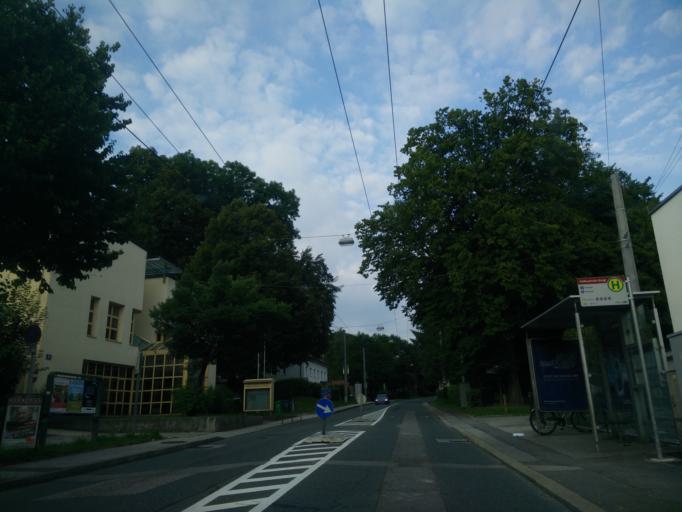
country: AT
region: Salzburg
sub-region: Salzburg Stadt
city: Salzburg
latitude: 47.8132
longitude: 13.0726
